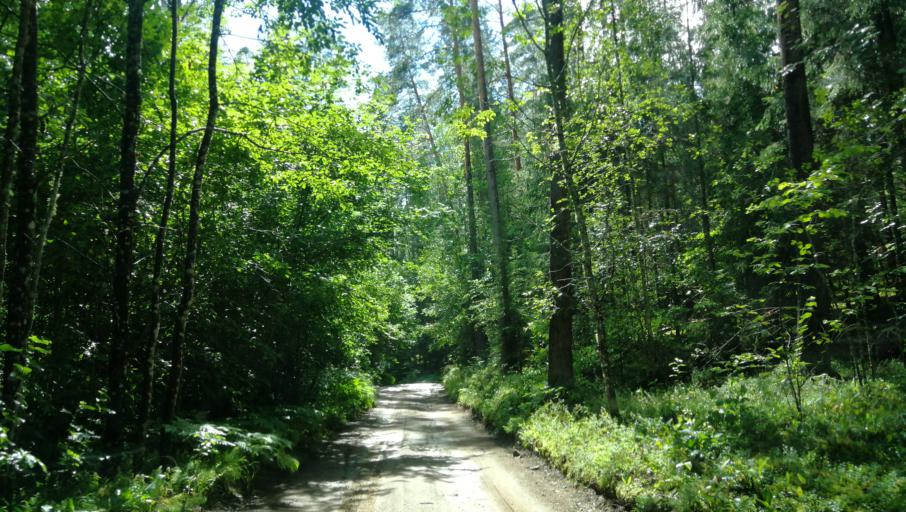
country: LV
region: Cesu Rajons
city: Cesis
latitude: 57.3085
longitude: 25.2143
